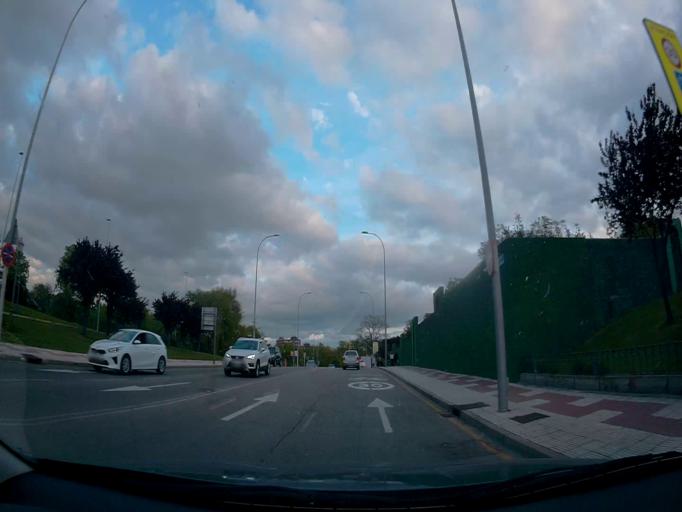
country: ES
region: Madrid
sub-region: Provincia de Madrid
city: Alcorcon
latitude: 40.3416
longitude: -3.8416
